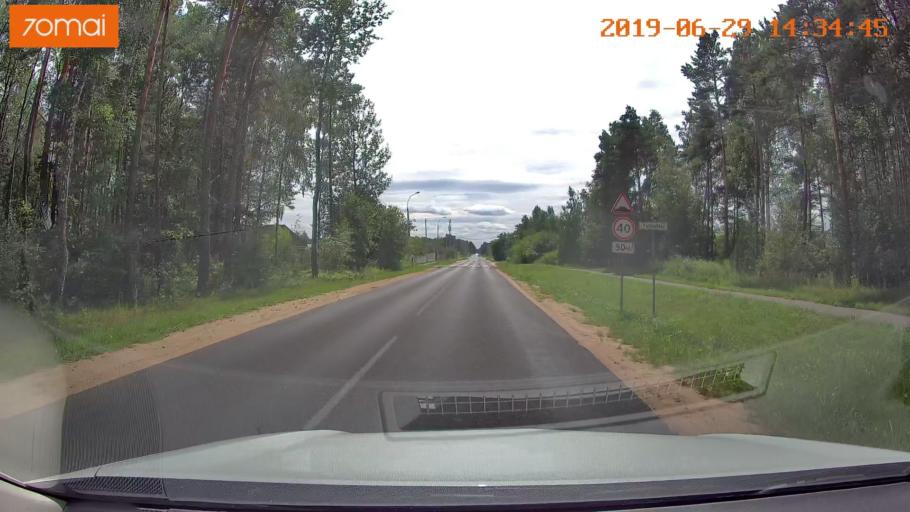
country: BY
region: Minsk
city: Starobin
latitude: 52.7650
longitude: 27.4902
